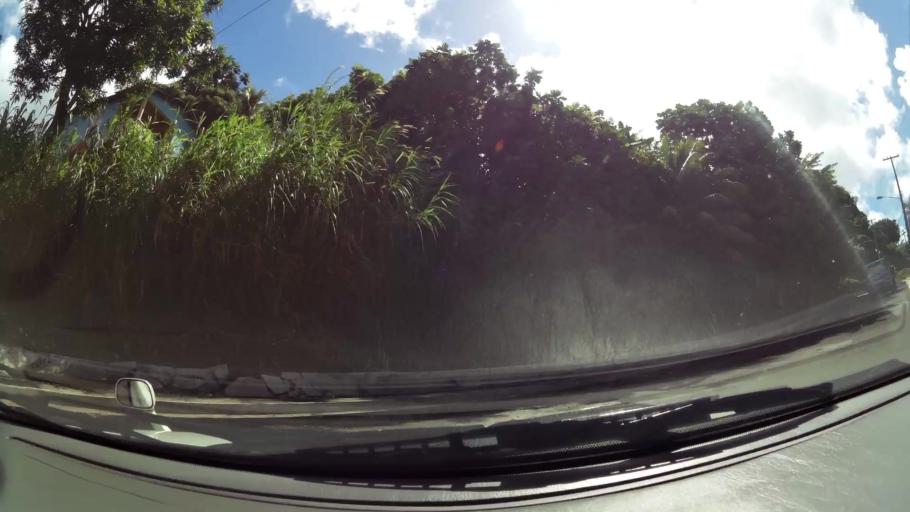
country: VC
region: Saint George
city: Kingstown Park
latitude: 13.1751
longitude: -61.2355
